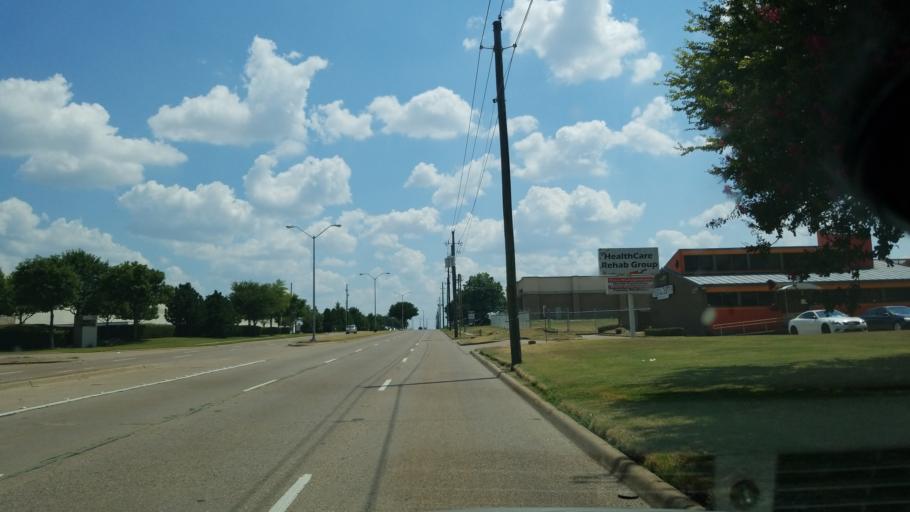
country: US
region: Texas
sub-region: Dallas County
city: Duncanville
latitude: 32.6839
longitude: -96.8829
